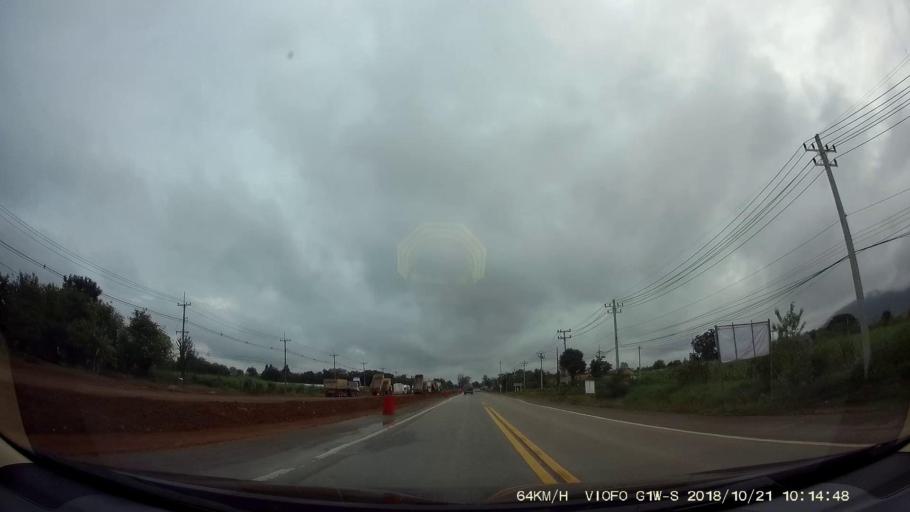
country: TH
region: Chaiyaphum
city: Phu Khiao
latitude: 16.3459
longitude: 102.1597
